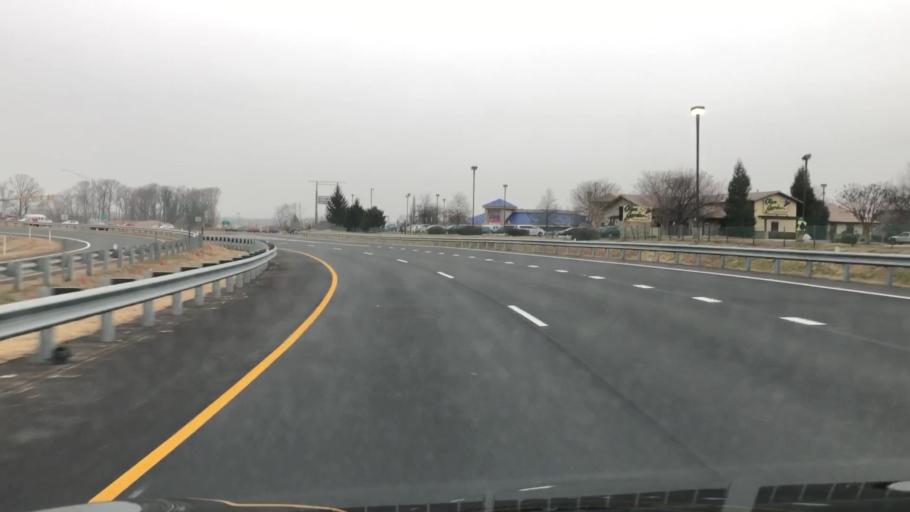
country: US
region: Virginia
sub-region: Stafford County
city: Falmouth
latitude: 38.2979
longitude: -77.5075
